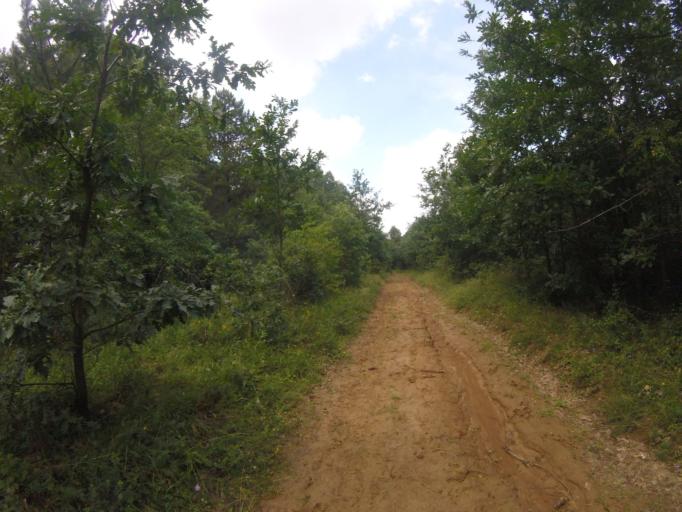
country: SK
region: Nitriansky
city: Sahy
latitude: 48.0236
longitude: 18.9489
